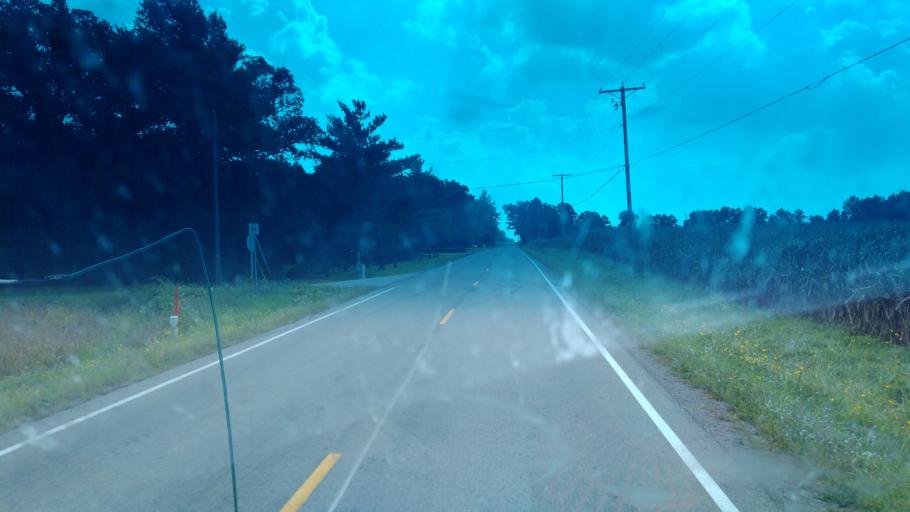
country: US
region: Ohio
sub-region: Hardin County
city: Ada
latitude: 40.7152
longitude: -83.7851
